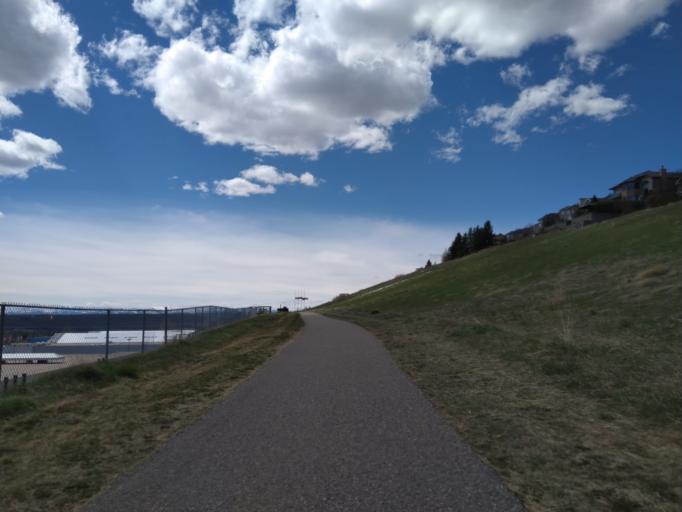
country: CA
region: Alberta
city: Calgary
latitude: 51.0212
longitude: -114.1702
